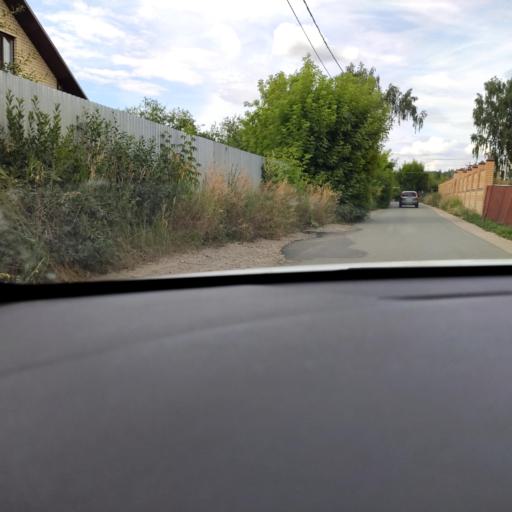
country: RU
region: Tatarstan
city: Staroye Arakchino
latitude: 55.8047
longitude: 48.9430
